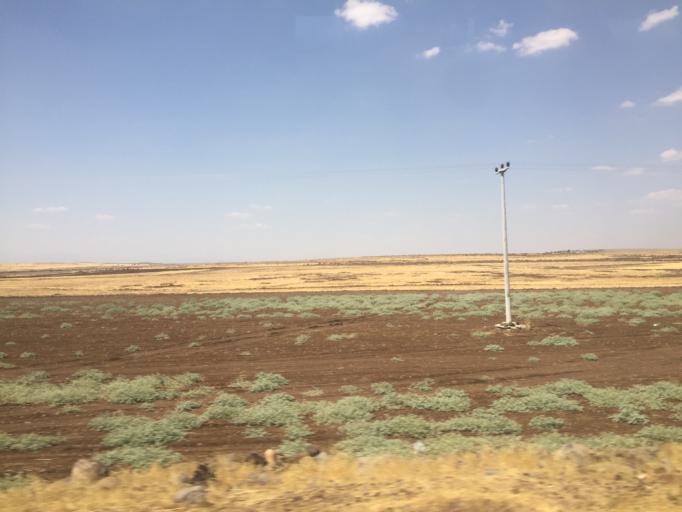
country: TR
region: Sanliurfa
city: Siverek
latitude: 37.7686
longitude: 39.4328
